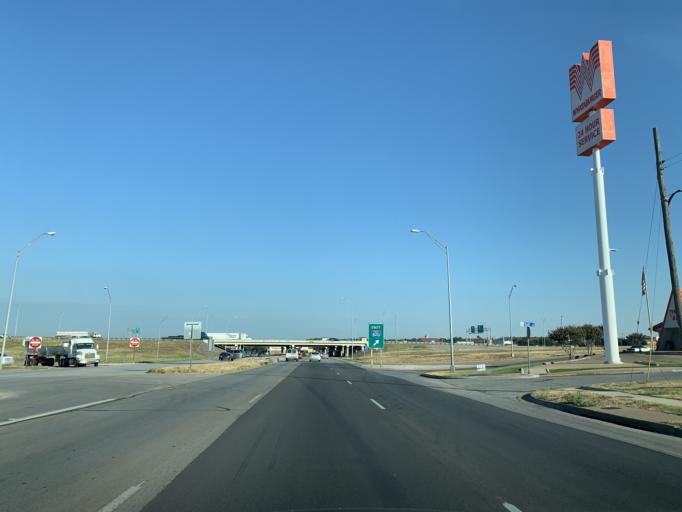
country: US
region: Texas
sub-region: Tarrant County
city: Sansom Park
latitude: 32.8073
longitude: -97.4162
